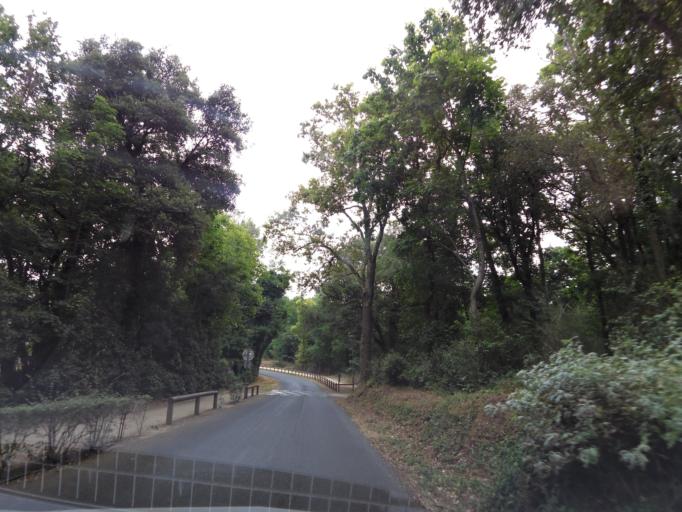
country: FR
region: Pays de la Loire
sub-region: Departement de la Vendee
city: Longeville-sur-Mer
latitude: 46.4073
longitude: -1.4936
